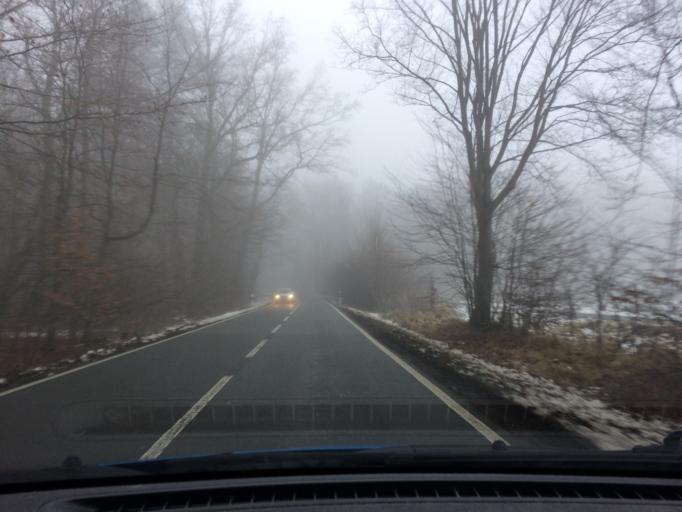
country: DE
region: Schleswig-Holstein
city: Kollow
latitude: 53.4848
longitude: 10.4667
